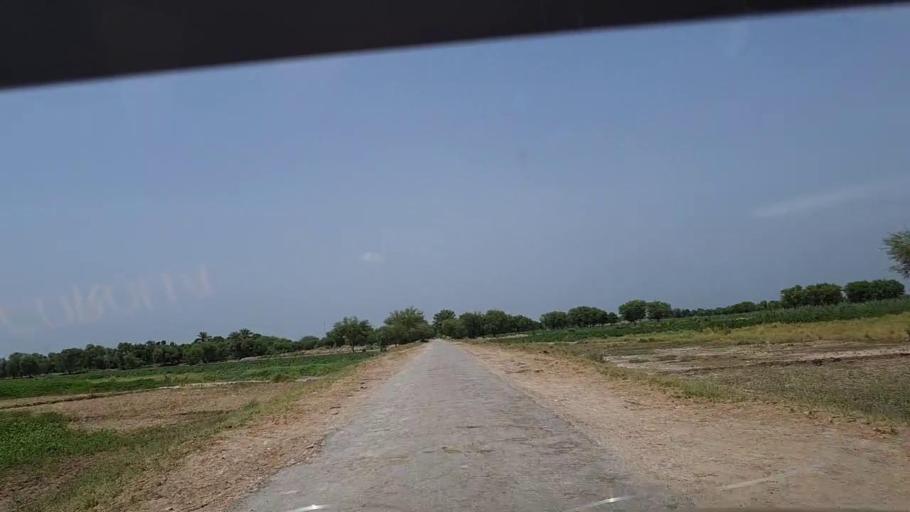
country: PK
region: Sindh
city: Khanpur
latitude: 27.7942
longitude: 69.4549
